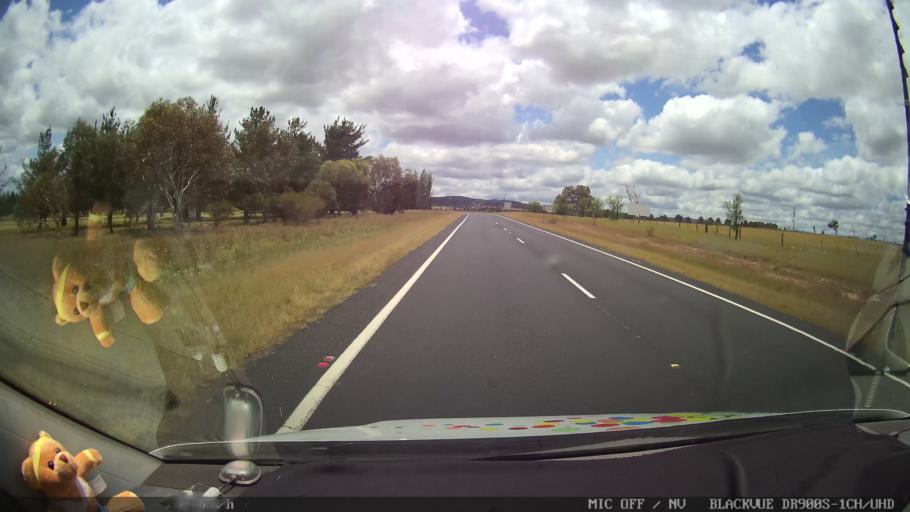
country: AU
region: New South Wales
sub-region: Glen Innes Severn
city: Glen Innes
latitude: -29.4345
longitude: 151.8503
